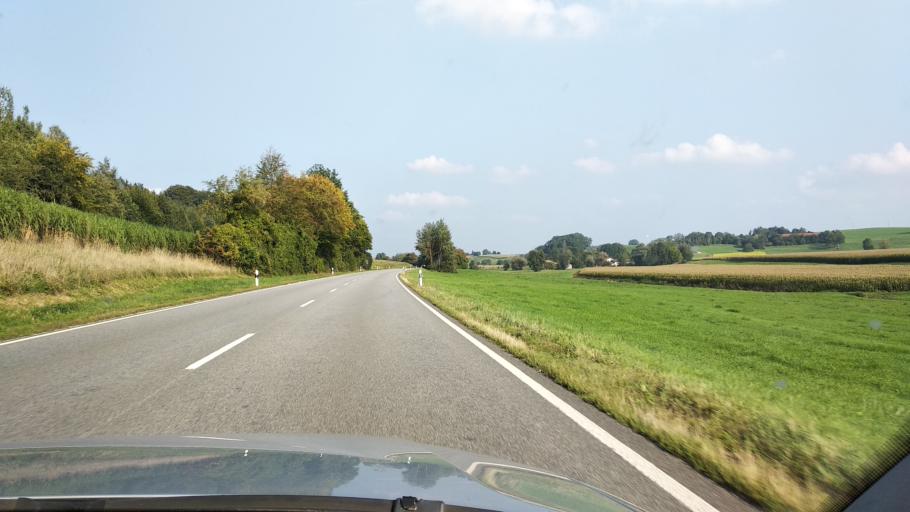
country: DE
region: Bavaria
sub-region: Upper Bavaria
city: Steinhoring
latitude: 48.0853
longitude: 12.0119
